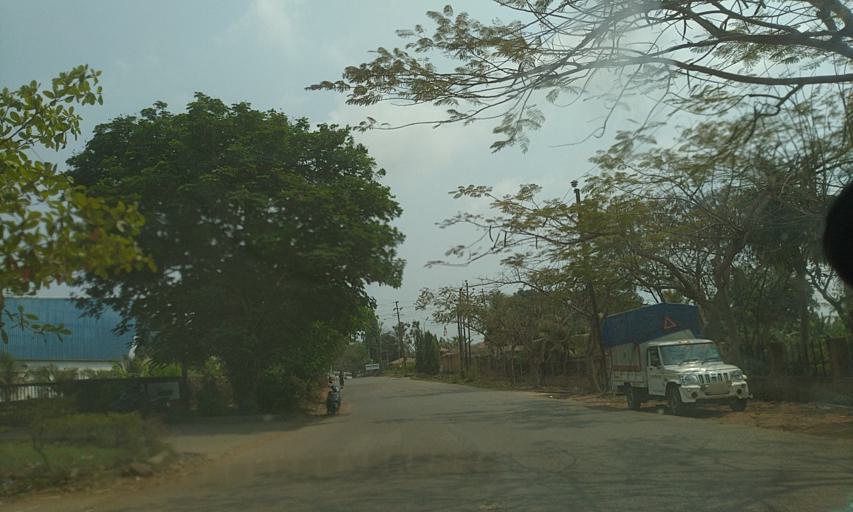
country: IN
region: Goa
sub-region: South Goa
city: Sancoale
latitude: 15.3741
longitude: 73.9277
